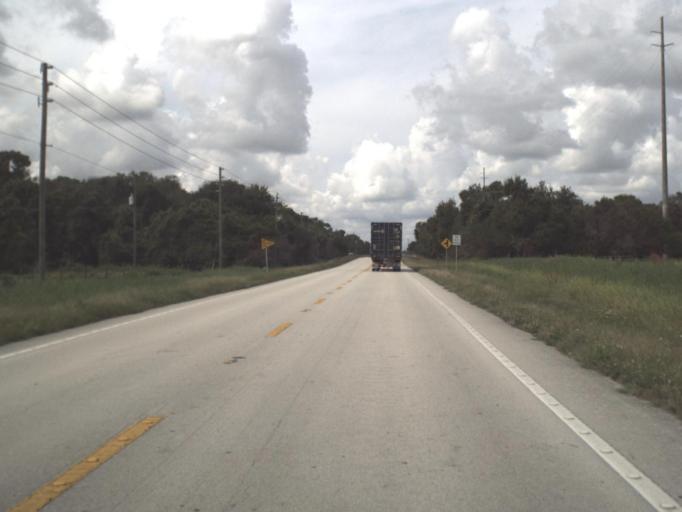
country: US
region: Florida
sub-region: Okeechobee County
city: Okeechobee
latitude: 27.2436
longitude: -80.8940
